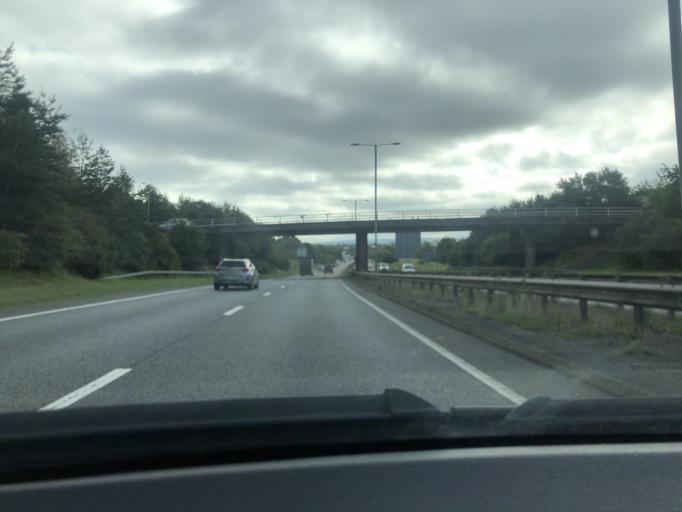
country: GB
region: England
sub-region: Devon
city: Topsham
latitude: 50.7307
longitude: -3.4456
